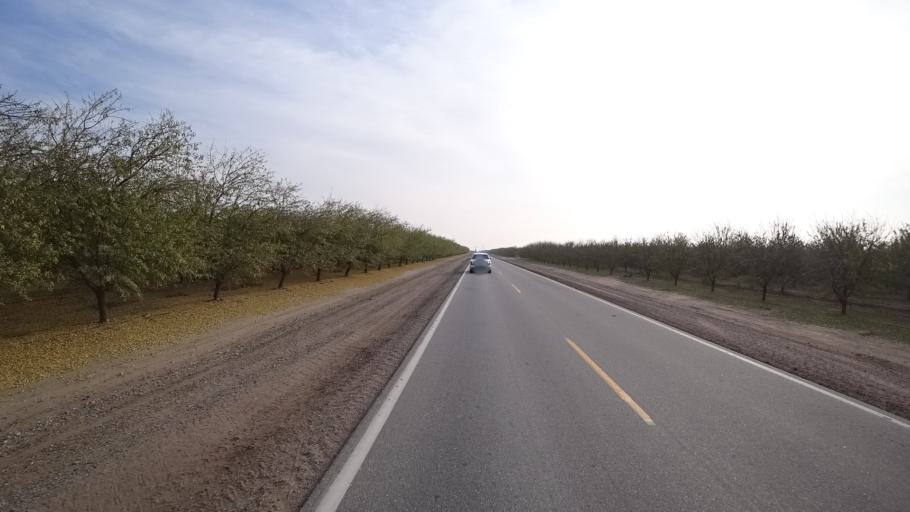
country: US
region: California
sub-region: Kern County
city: Greenacres
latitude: 35.2757
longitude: -119.1283
